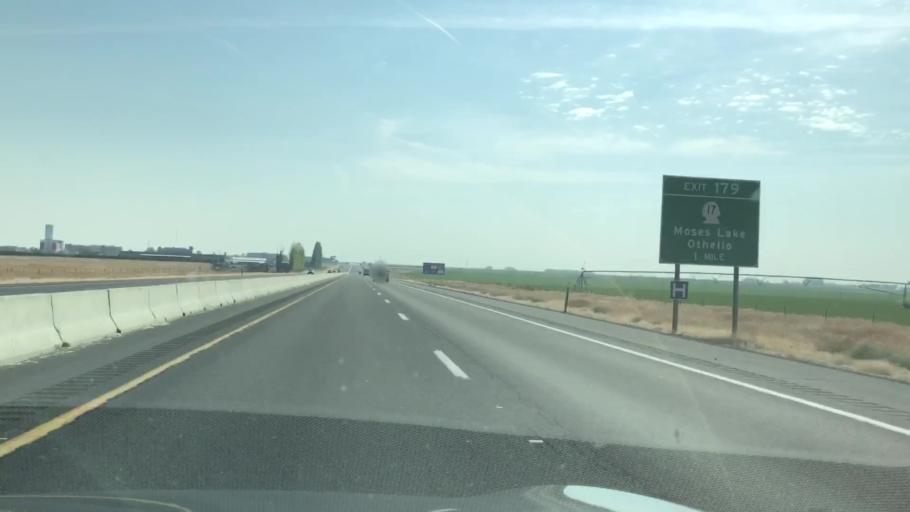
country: US
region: Washington
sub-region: Grant County
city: Moses Lake
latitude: 47.1015
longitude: -119.2686
